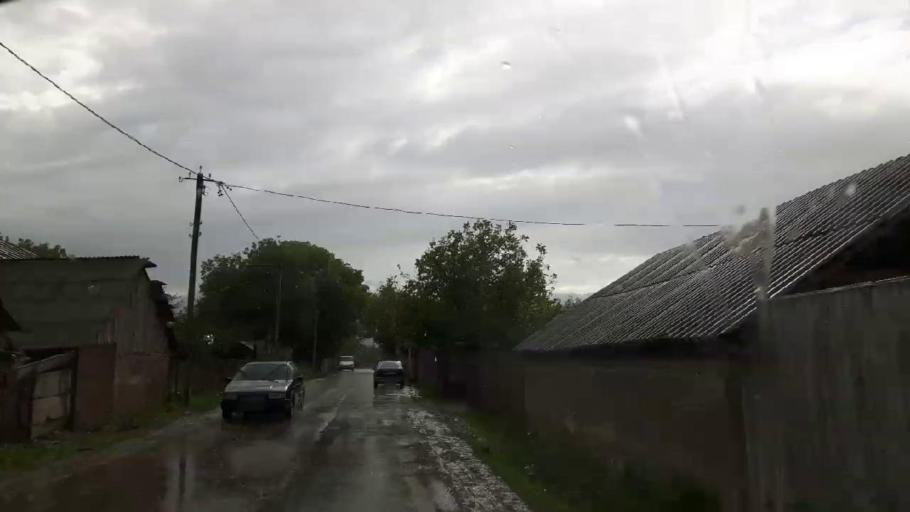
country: GE
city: Agara
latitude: 42.0067
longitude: 43.7640
